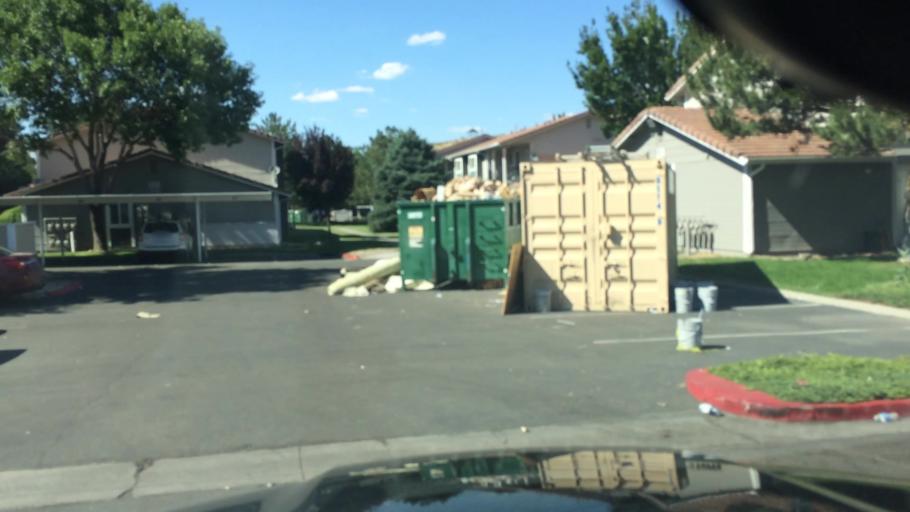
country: US
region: Nevada
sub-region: Washoe County
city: Sparks
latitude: 39.4500
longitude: -119.7695
